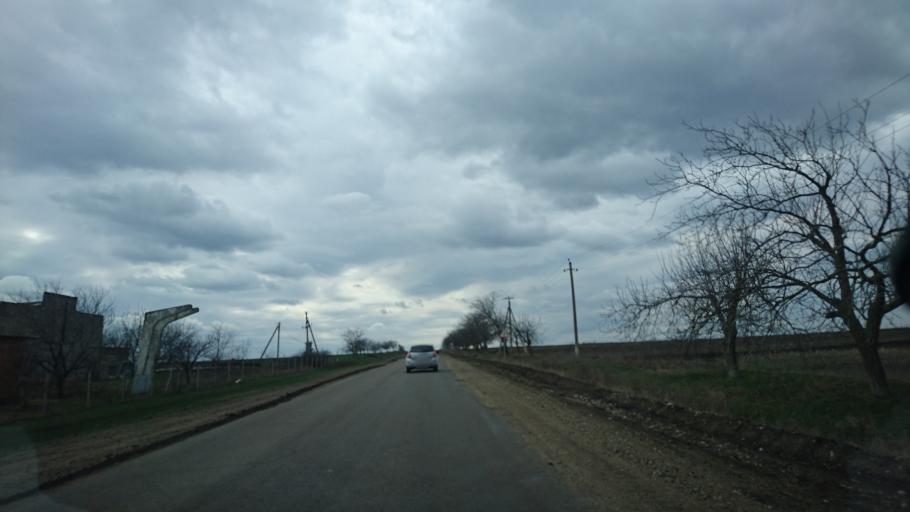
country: MD
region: Gagauzia
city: Comrat
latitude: 46.3078
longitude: 28.6121
